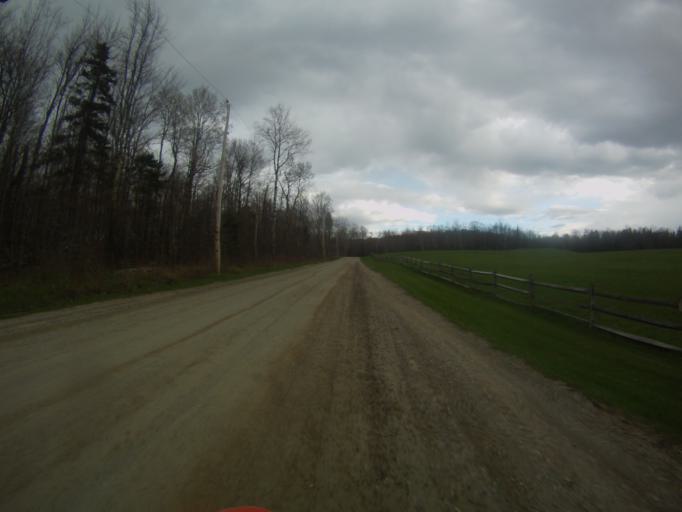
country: US
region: Vermont
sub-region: Addison County
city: Bristol
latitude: 44.0599
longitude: -73.0075
